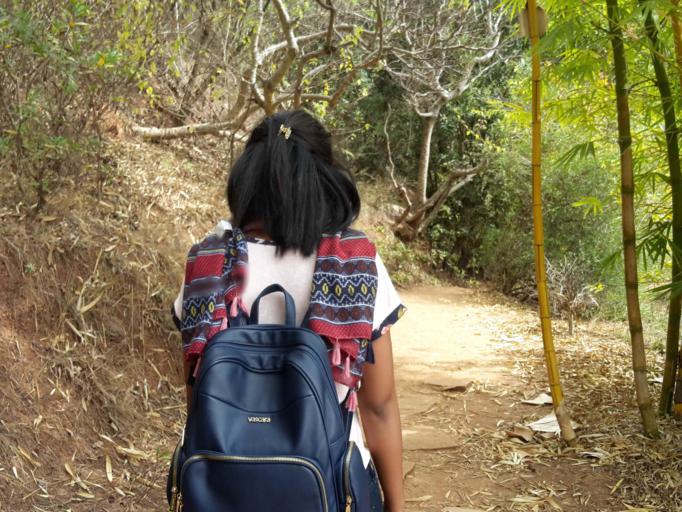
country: MG
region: Analamanga
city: Antananarivo
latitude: -18.9523
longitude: 47.3585
